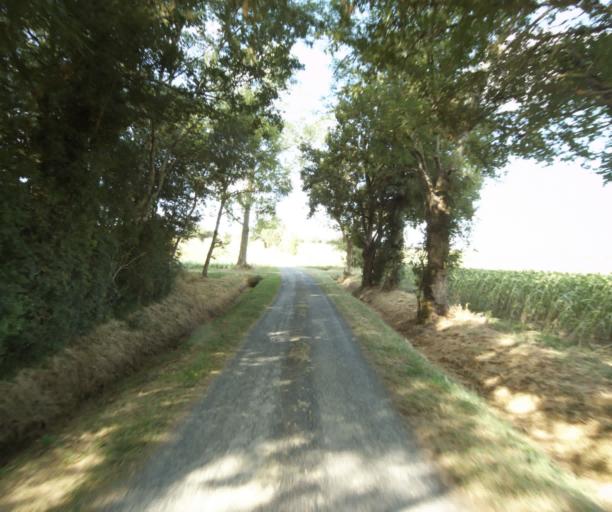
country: FR
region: Midi-Pyrenees
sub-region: Departement du Tarn
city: Puylaurens
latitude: 43.5322
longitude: 1.9824
